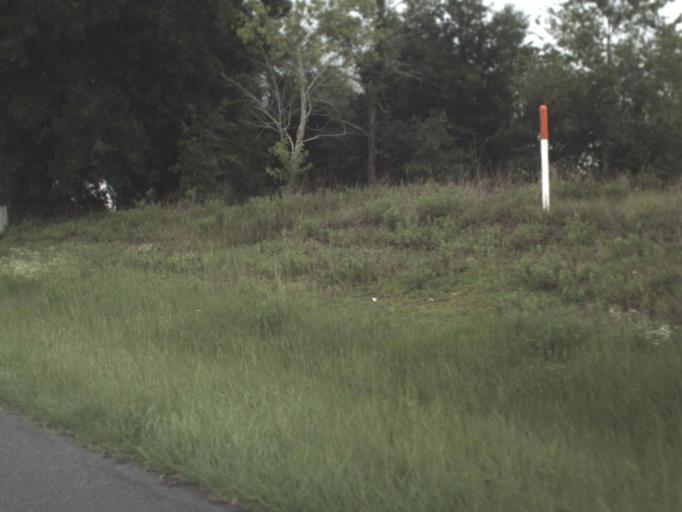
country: US
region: Florida
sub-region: Levy County
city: Williston
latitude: 29.3048
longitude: -82.4495
